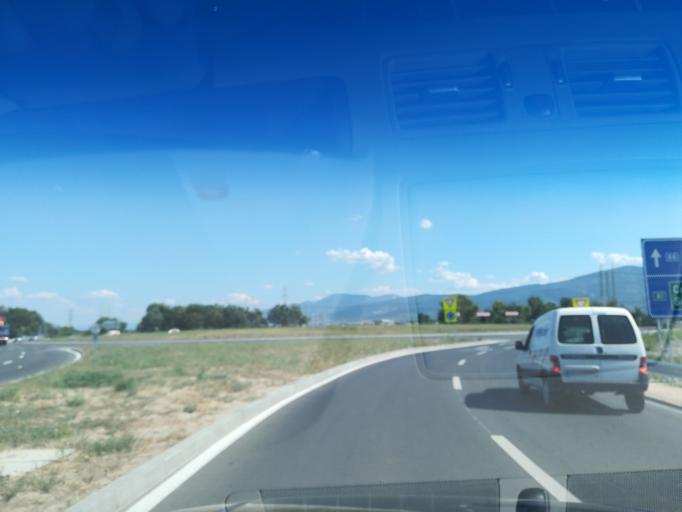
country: BG
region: Plovdiv
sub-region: Obshtina Plovdiv
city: Plovdiv
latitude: 42.1001
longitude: 24.7875
